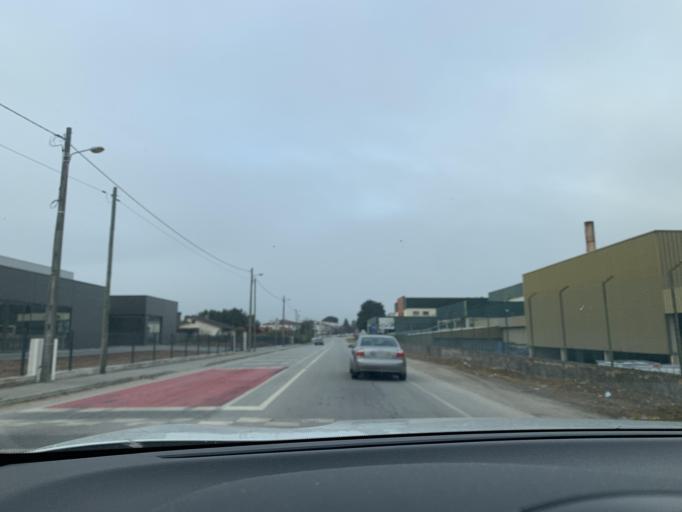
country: PT
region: Viseu
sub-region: Viseu
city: Rio de Loba
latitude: 40.6270
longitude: -7.8851
